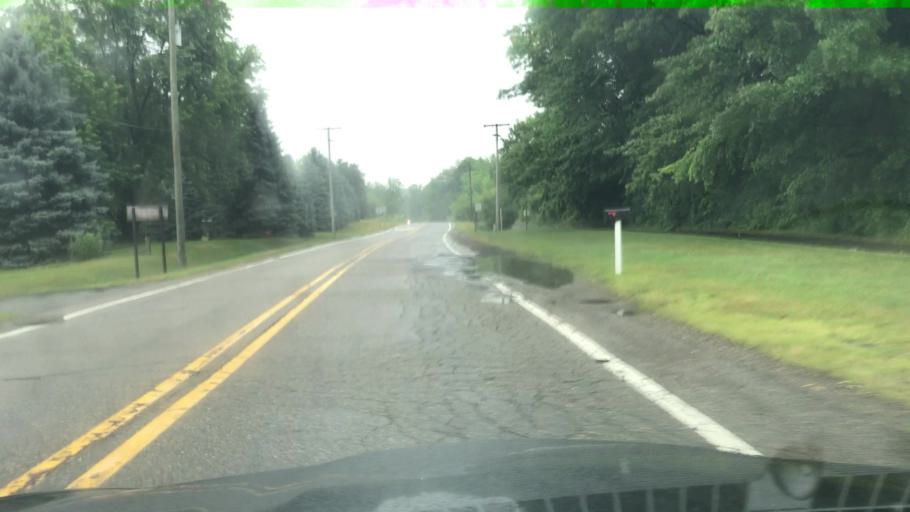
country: US
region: Michigan
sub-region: Oakland County
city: Auburn Hills
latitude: 42.7248
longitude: -83.2852
